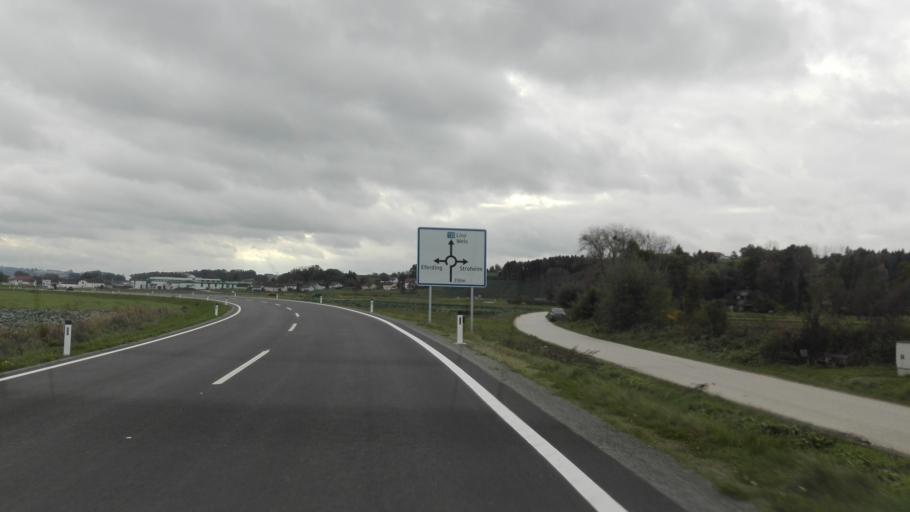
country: AT
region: Upper Austria
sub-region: Politischer Bezirk Urfahr-Umgebung
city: Feldkirchen an der Donau
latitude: 48.3209
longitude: 14.0076
